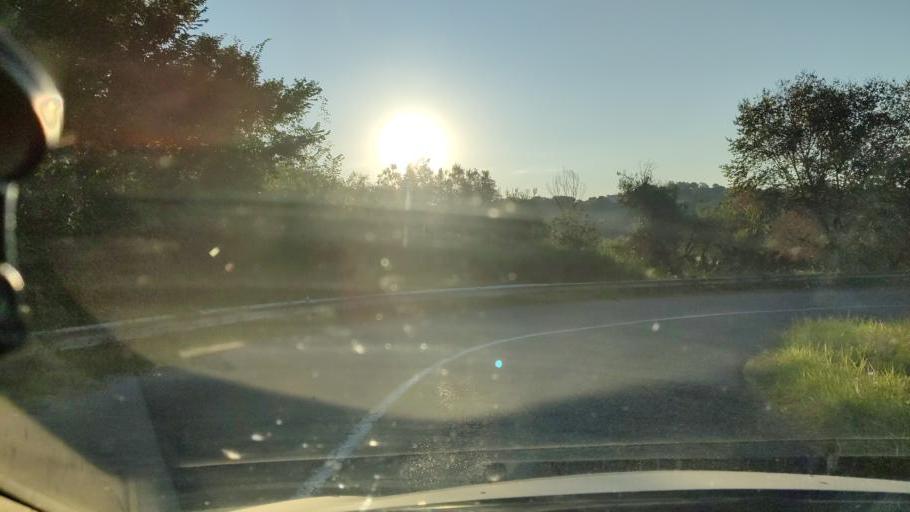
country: IT
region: Umbria
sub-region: Provincia di Terni
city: Giove
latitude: 42.5051
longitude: 12.3248
